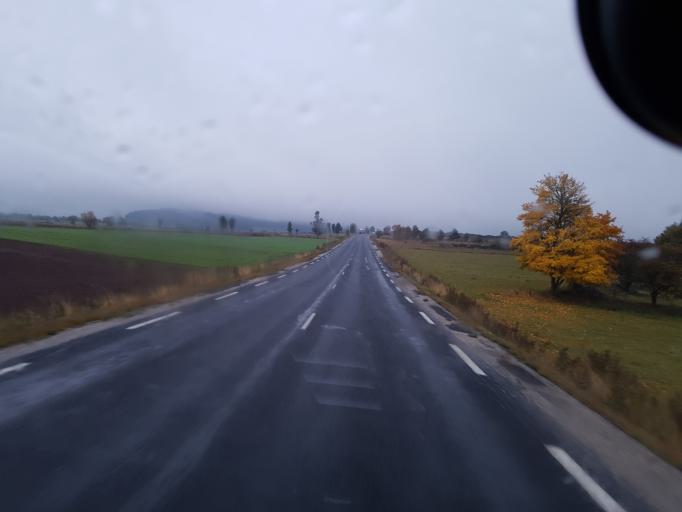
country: FR
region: Languedoc-Roussillon
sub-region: Departement de la Lozere
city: Langogne
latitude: 44.8448
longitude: 3.8562
